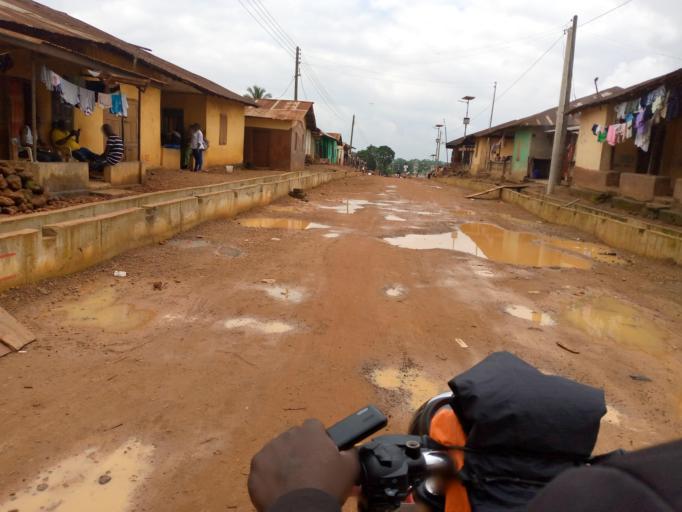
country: SL
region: Eastern Province
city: Kenema
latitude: 7.8725
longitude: -11.1886
